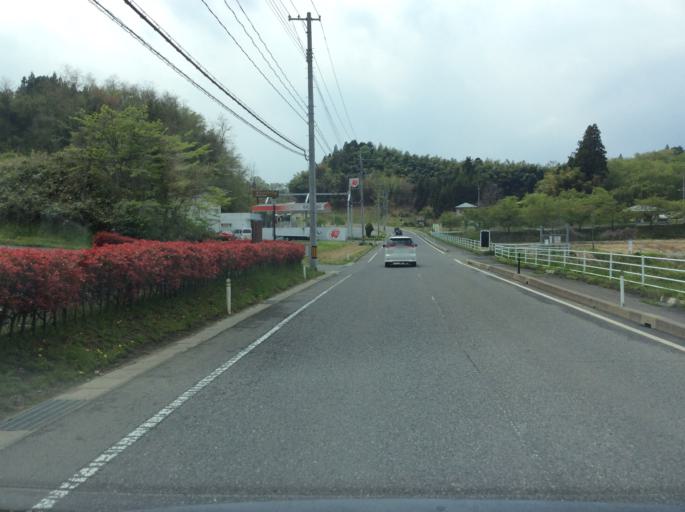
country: JP
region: Fukushima
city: Miharu
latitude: 37.3981
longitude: 140.4956
